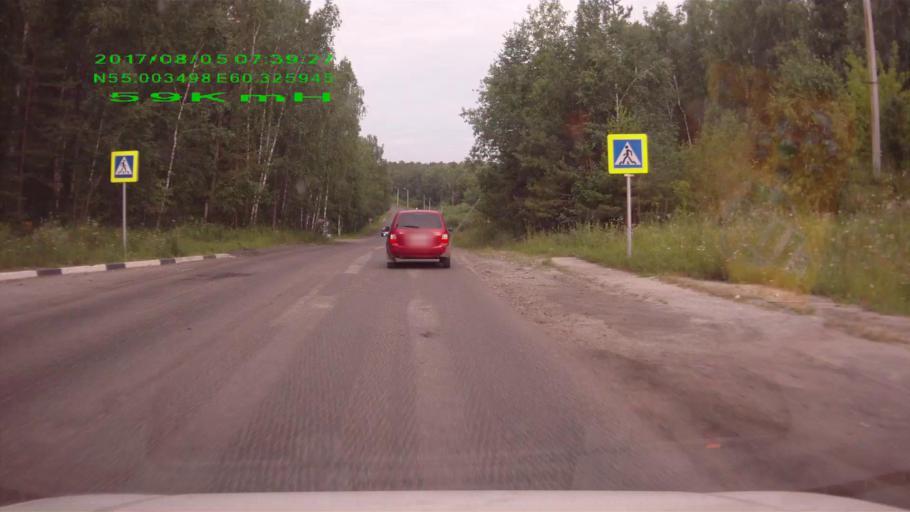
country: RU
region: Chelyabinsk
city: Chebarkul'
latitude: 55.0036
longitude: 60.3257
